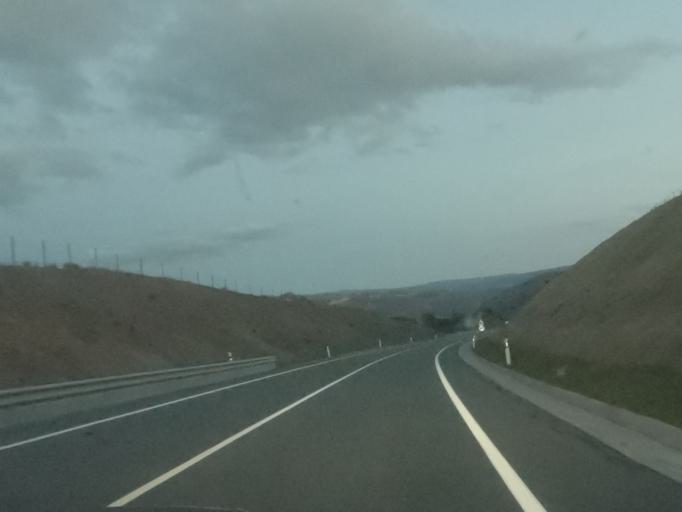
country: PT
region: Braganca
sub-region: Alfandega da Fe
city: Alfandega da Fe
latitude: 41.3226
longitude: -6.9326
